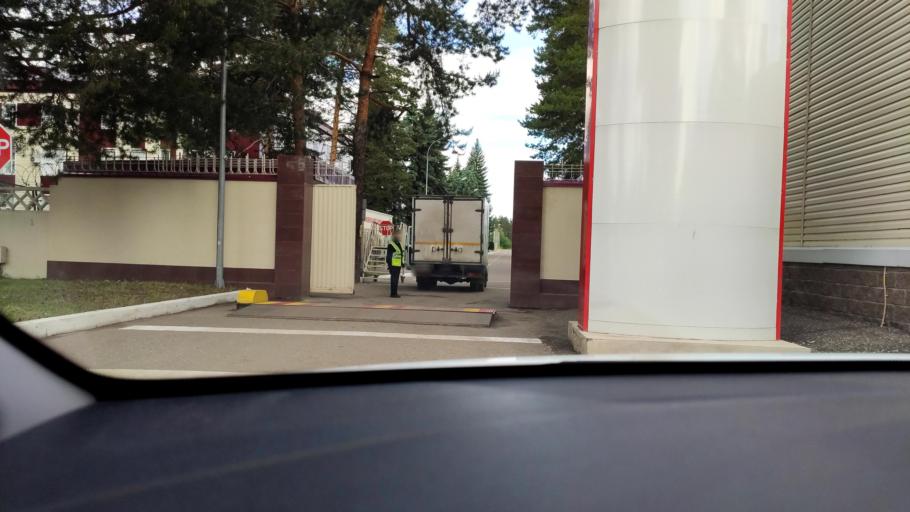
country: RU
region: Tatarstan
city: Vysokaya Gora
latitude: 55.8723
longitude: 49.2156
